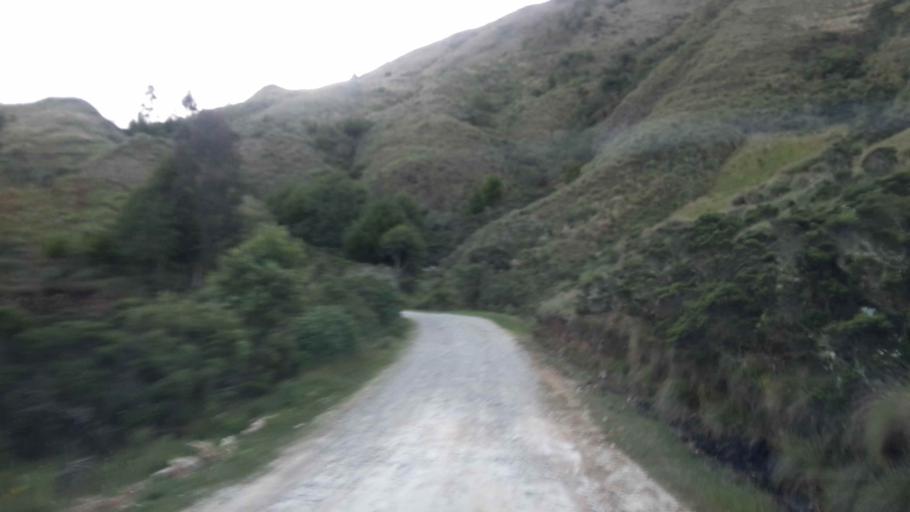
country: BO
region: Cochabamba
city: Colomi
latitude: -17.2409
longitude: -65.9056
